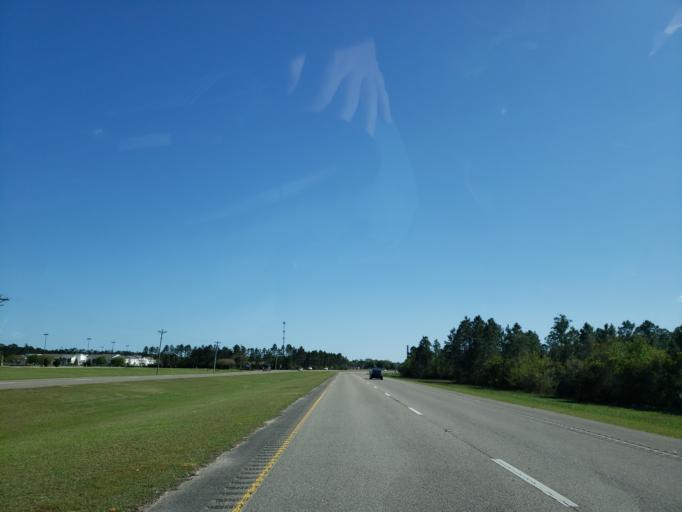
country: US
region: Mississippi
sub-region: Harrison County
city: West Gulfport
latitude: 30.4645
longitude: -89.0272
